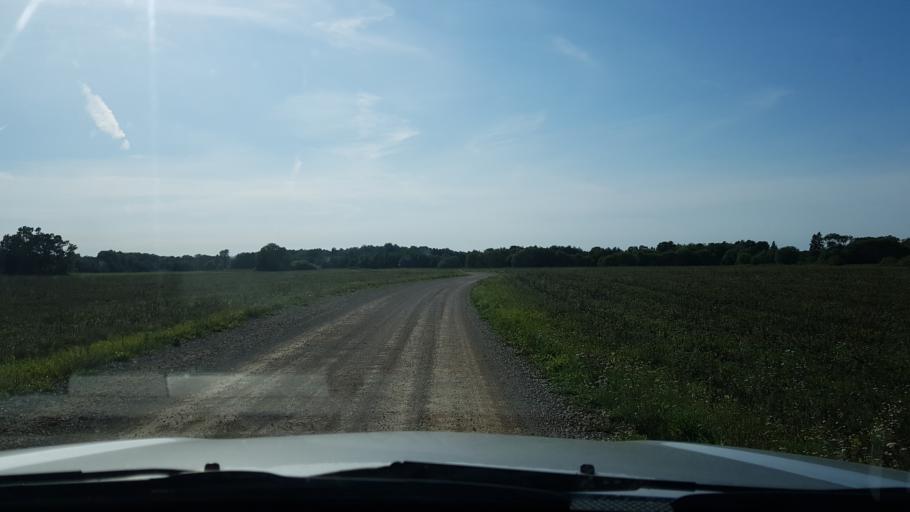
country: EE
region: Ida-Virumaa
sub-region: Narva-Joesuu linn
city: Narva-Joesuu
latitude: 59.4078
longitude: 28.0000
